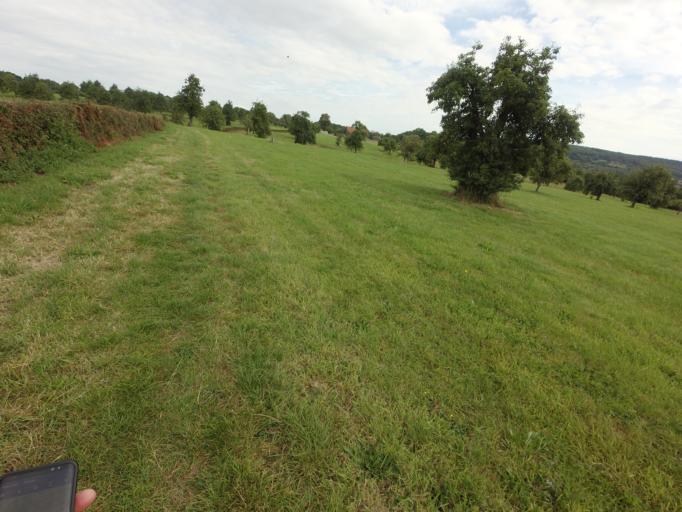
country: BE
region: Wallonia
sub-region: Province de Liege
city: Plombieres
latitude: 50.7555
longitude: 5.9209
